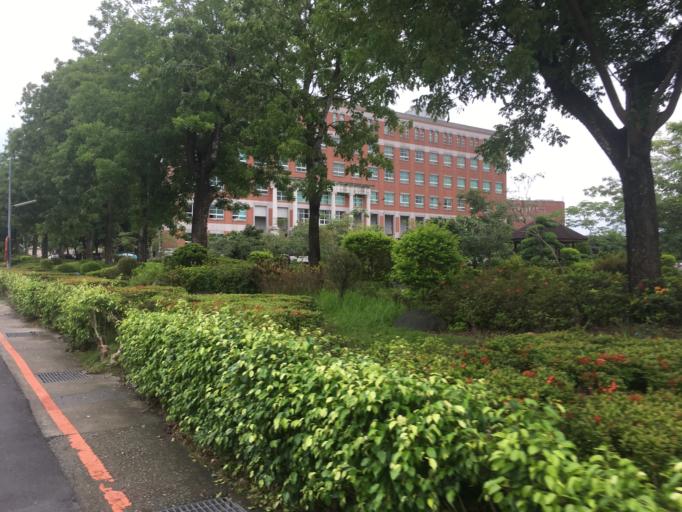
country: TW
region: Taiwan
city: Zhongxing New Village
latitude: 24.0484
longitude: 120.6868
